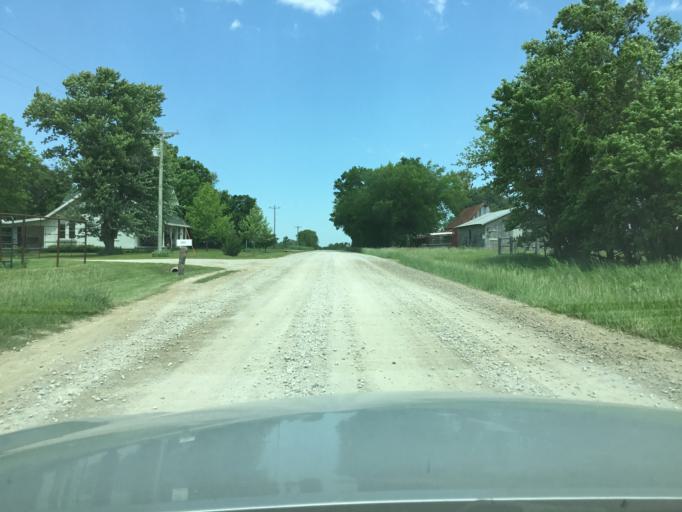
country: US
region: Kansas
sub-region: Montgomery County
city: Independence
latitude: 37.1012
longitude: -95.7829
